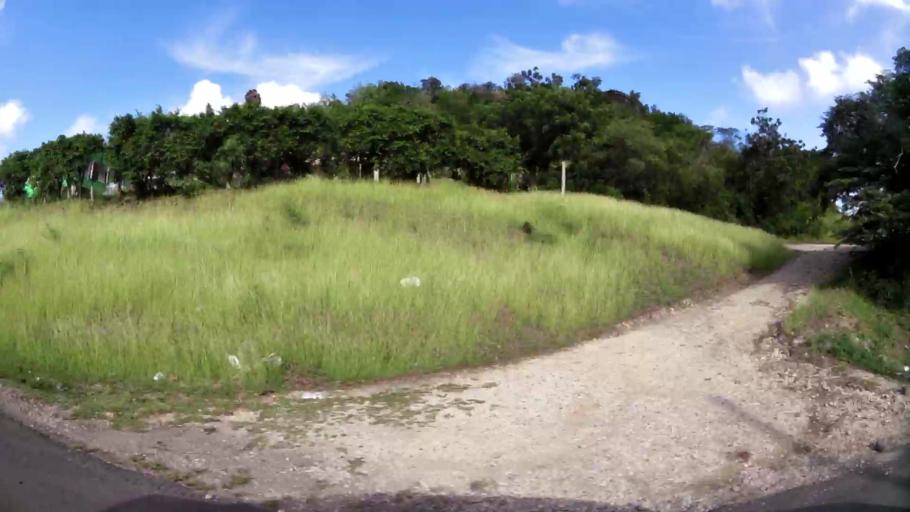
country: AG
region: Saint Paul
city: Liberta
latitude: 17.0307
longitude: -61.7875
